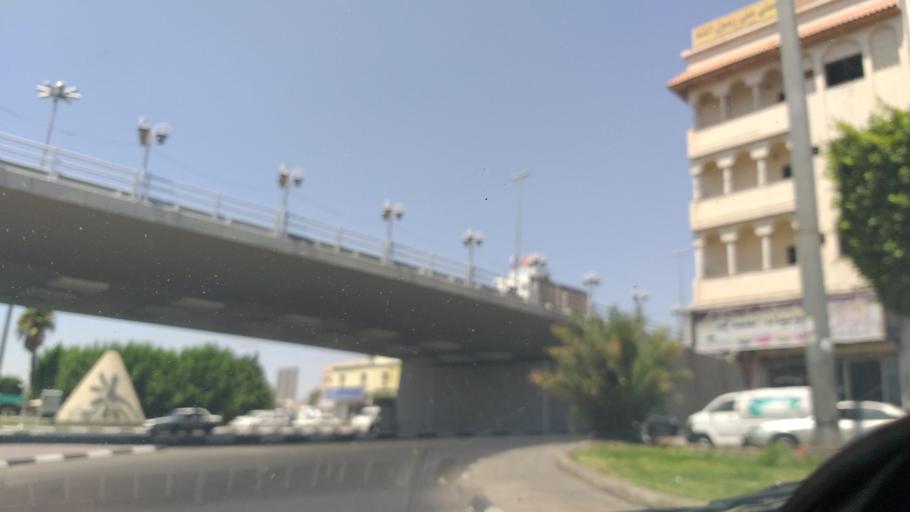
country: SA
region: Makkah
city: Ta'if
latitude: 21.2675
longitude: 40.4168
